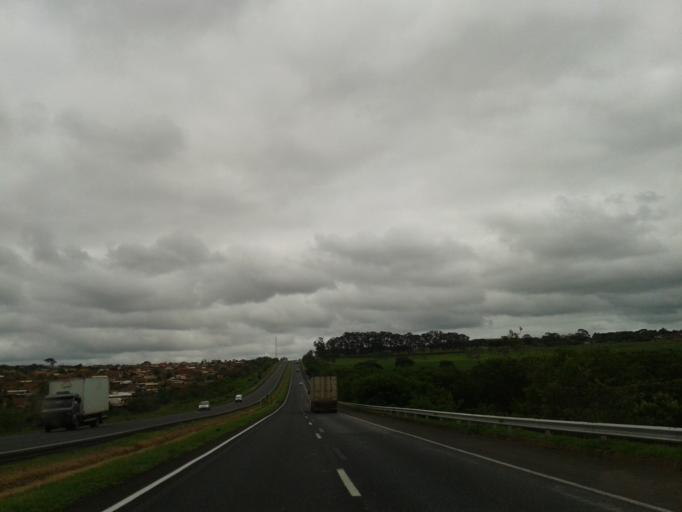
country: BR
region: Minas Gerais
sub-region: Uberlandia
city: Uberlandia
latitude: -18.9580
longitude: -48.2164
